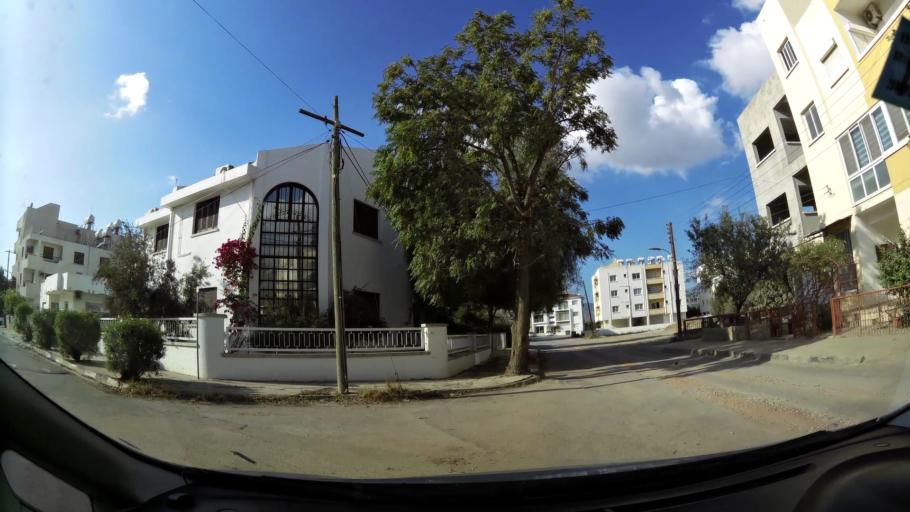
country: CY
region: Lefkosia
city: Nicosia
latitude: 35.1992
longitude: 33.3629
